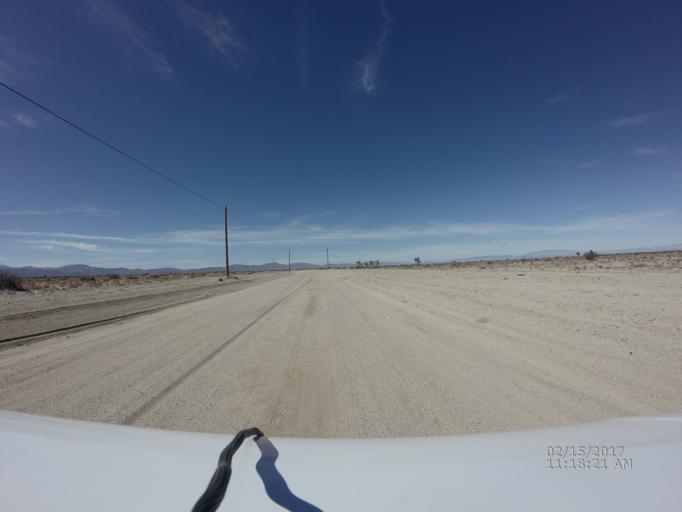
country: US
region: California
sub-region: Los Angeles County
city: Lake Los Angeles
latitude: 34.5872
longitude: -117.9149
